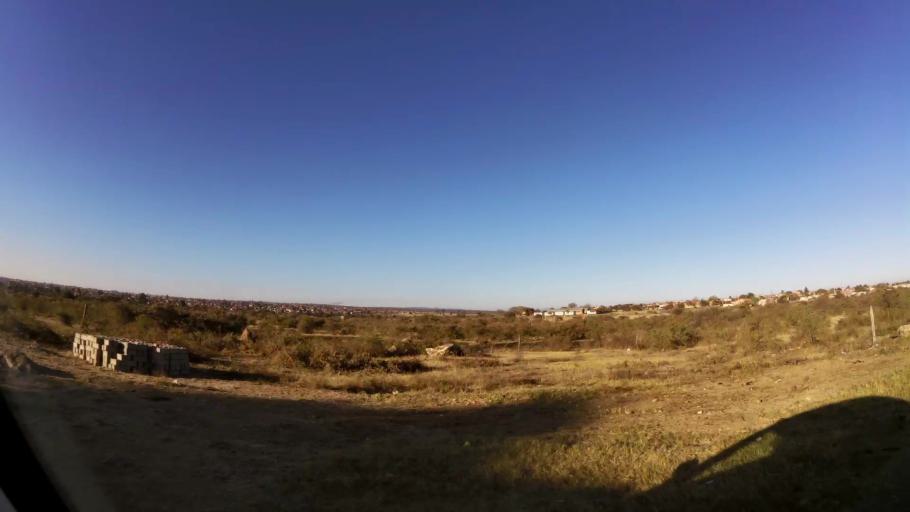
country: ZA
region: Limpopo
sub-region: Capricorn District Municipality
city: Polokwane
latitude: -23.8412
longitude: 29.3619
